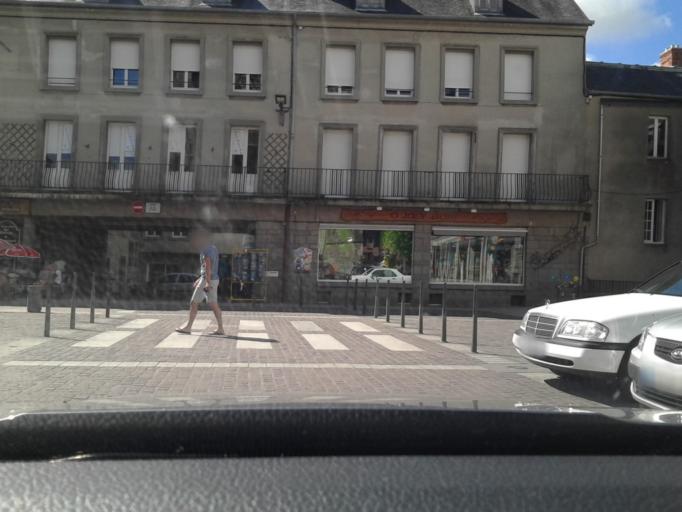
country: FR
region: Lower Normandy
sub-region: Departement de la Manche
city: Coutances
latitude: 49.0480
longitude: -1.4452
